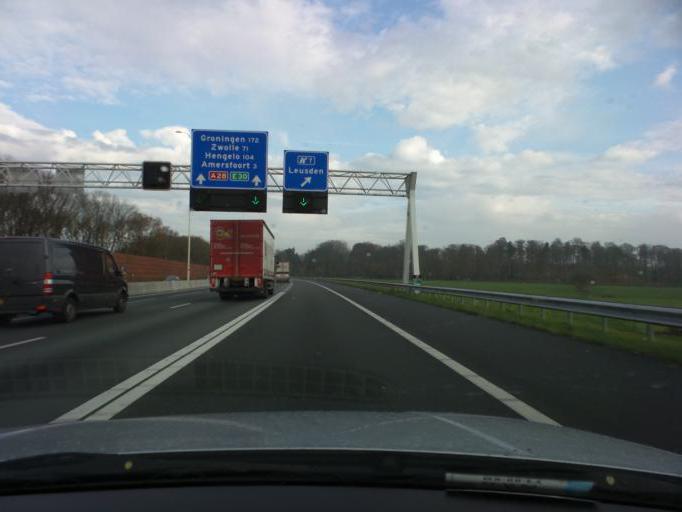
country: NL
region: Utrecht
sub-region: Gemeente Amersfoort
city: Randenbroek
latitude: 52.1370
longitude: 5.4018
